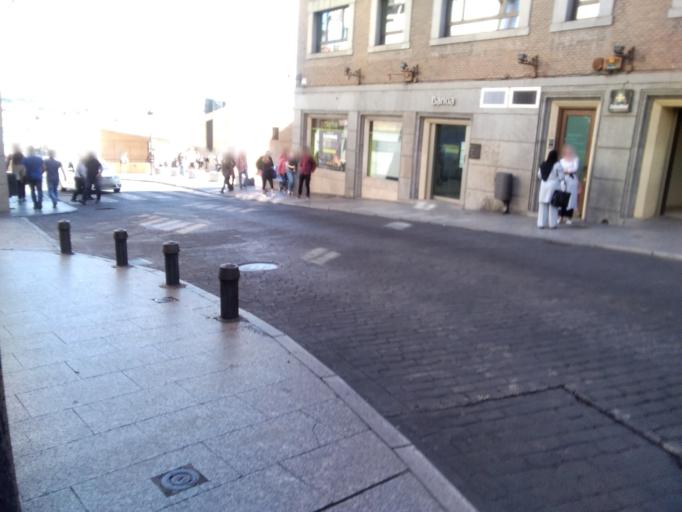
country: ES
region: Castille-La Mancha
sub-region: Province of Toledo
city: Toledo
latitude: 39.8603
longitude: -4.0211
